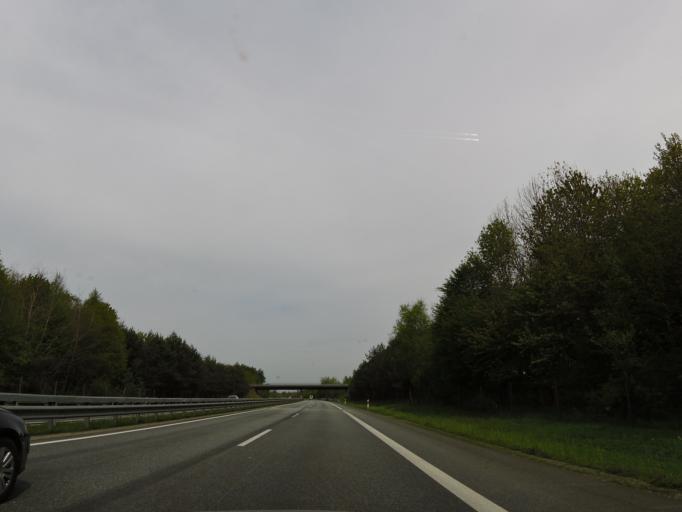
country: DE
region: Schleswig-Holstein
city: Ottenbuttel
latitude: 53.9850
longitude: 9.4910
